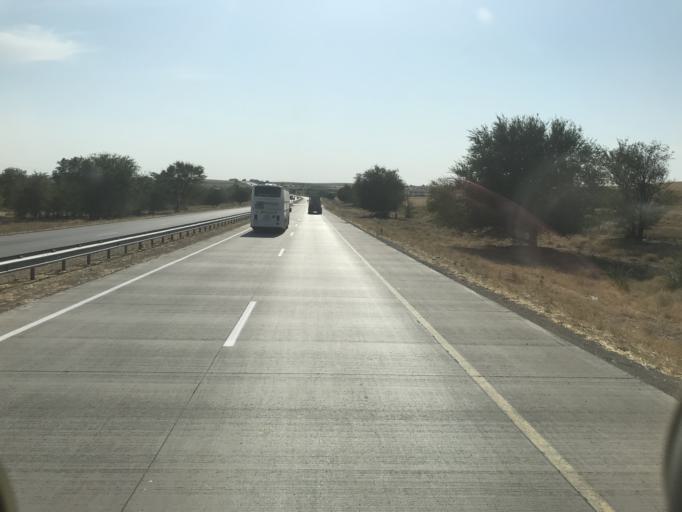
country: KZ
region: Ongtustik Qazaqstan
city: Sastobe
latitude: 42.4853
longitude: 69.9297
